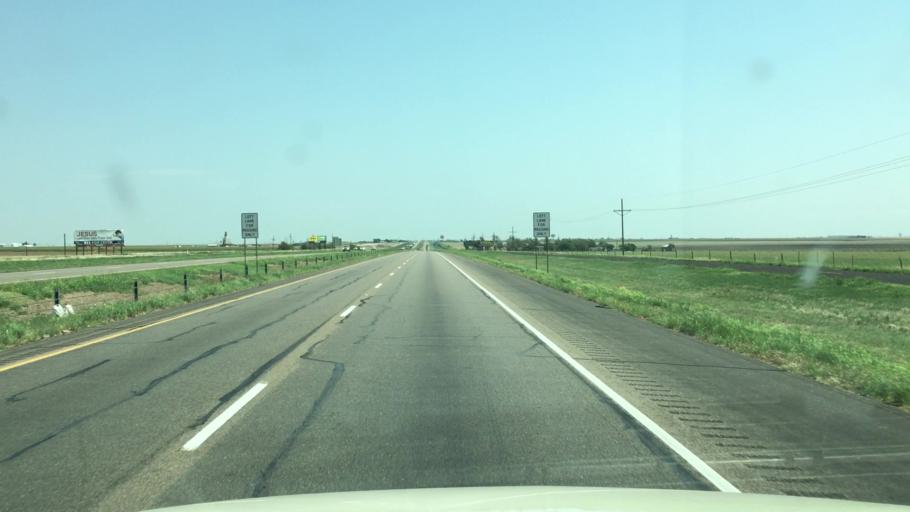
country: US
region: Texas
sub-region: Potter County
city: Bushland
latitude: 35.1907
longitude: -102.0445
